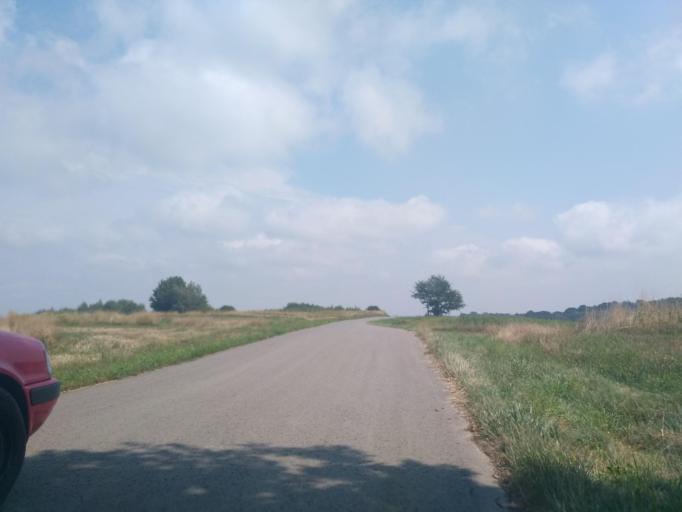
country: PL
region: Subcarpathian Voivodeship
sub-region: Powiat lancucki
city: Kraczkowa
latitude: 50.0266
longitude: 22.1559
